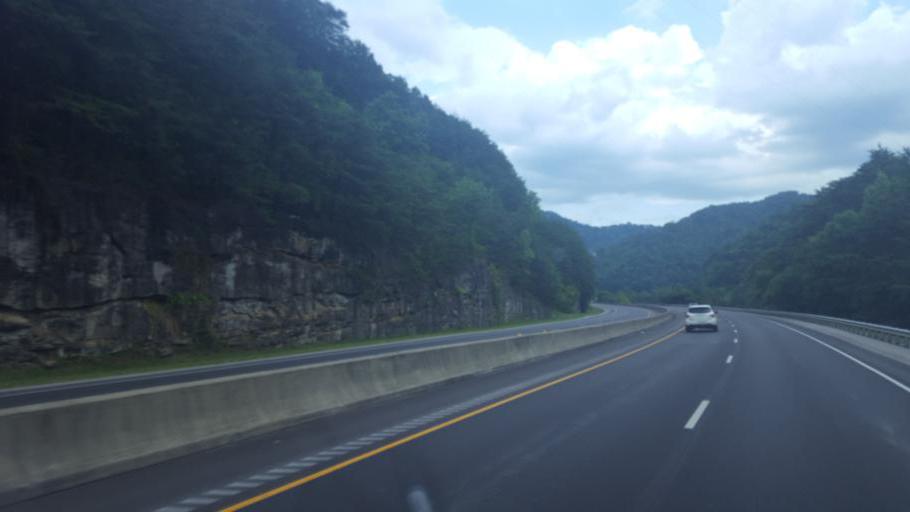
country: US
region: Kentucky
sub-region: Pike County
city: Pikeville
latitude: 37.3535
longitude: -82.5542
